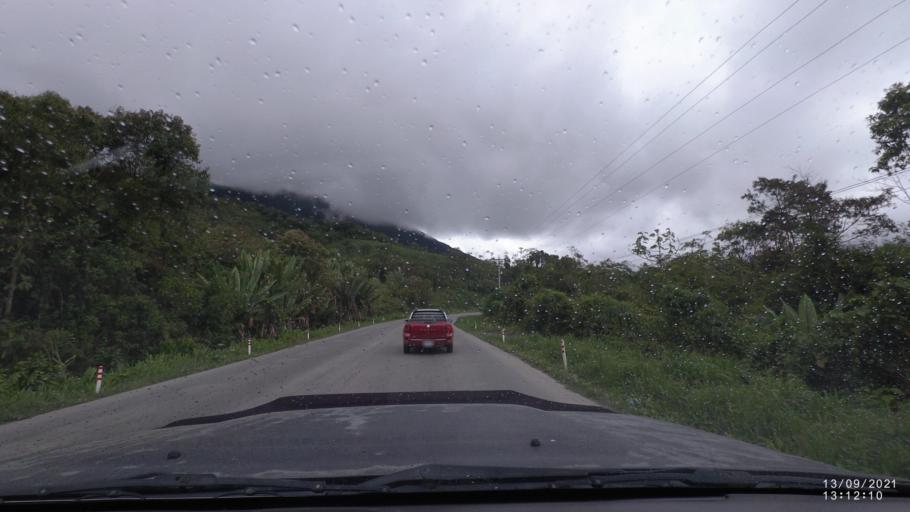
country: BO
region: Cochabamba
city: Colomi
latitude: -17.2011
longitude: -65.8350
